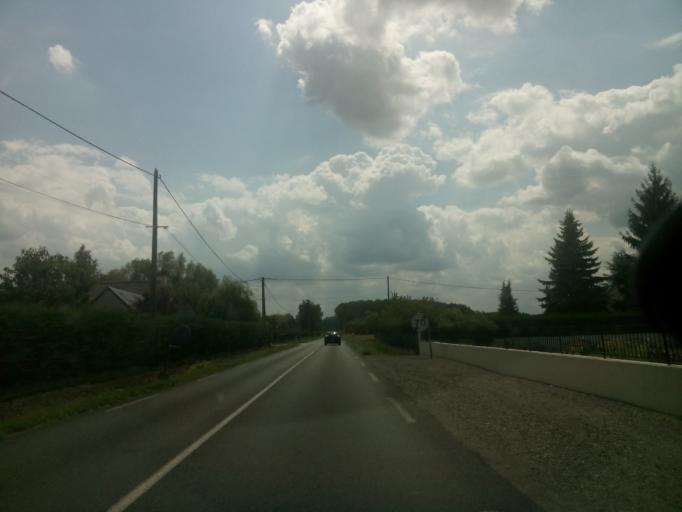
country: FR
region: Centre
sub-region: Departement d'Indre-et-Loire
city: Langeais
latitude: 47.3116
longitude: 0.4098
